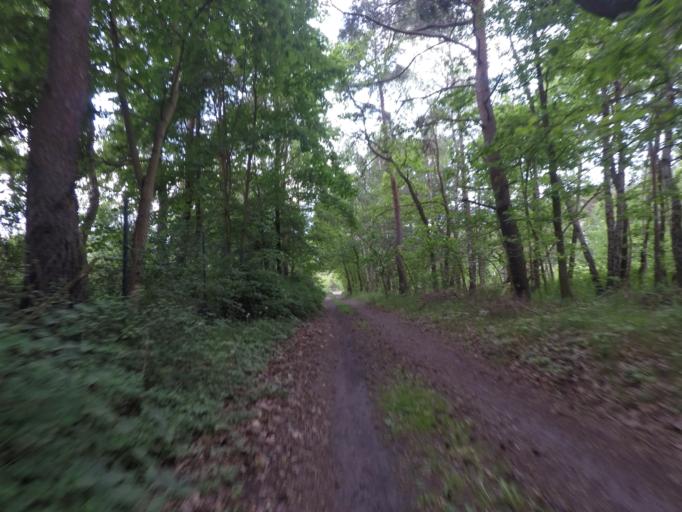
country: DE
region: Brandenburg
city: Eberswalde
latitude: 52.8440
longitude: 13.7535
